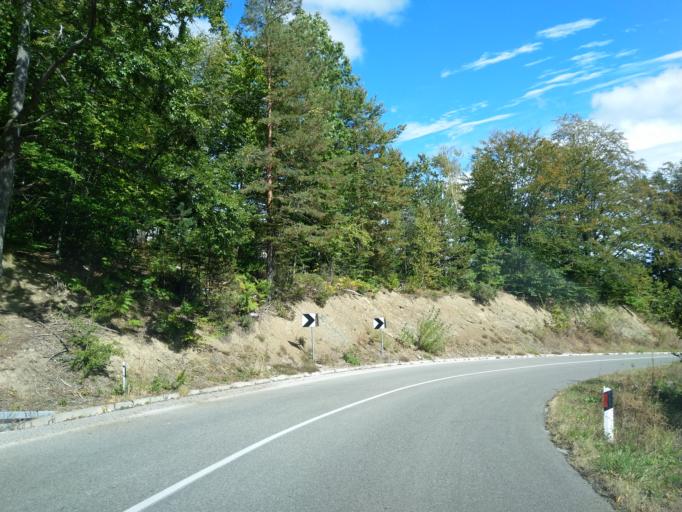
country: RS
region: Central Serbia
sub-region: Zlatiborski Okrug
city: Cajetina
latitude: 43.7185
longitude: 19.7828
